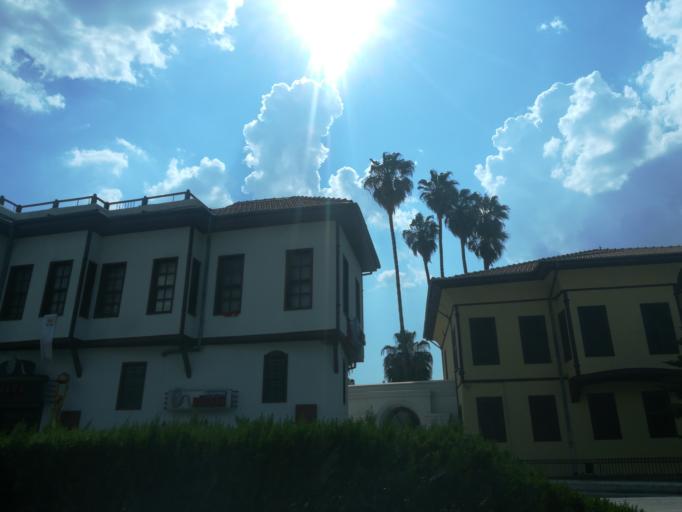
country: TR
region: Adana
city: Adana
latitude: 36.9886
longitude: 35.3320
